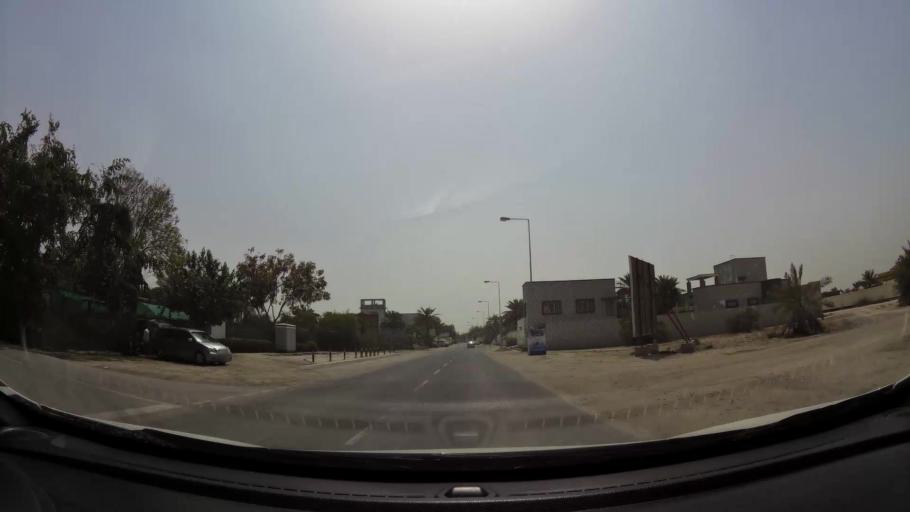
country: BH
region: Manama
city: Jidd Hafs
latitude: 26.2250
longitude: 50.4827
